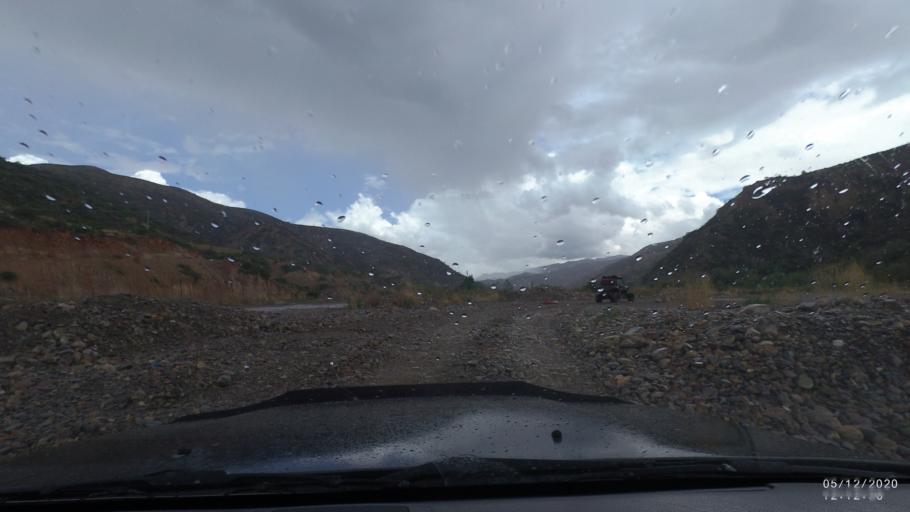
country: BO
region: Cochabamba
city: Sipe Sipe
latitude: -17.5636
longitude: -66.3768
